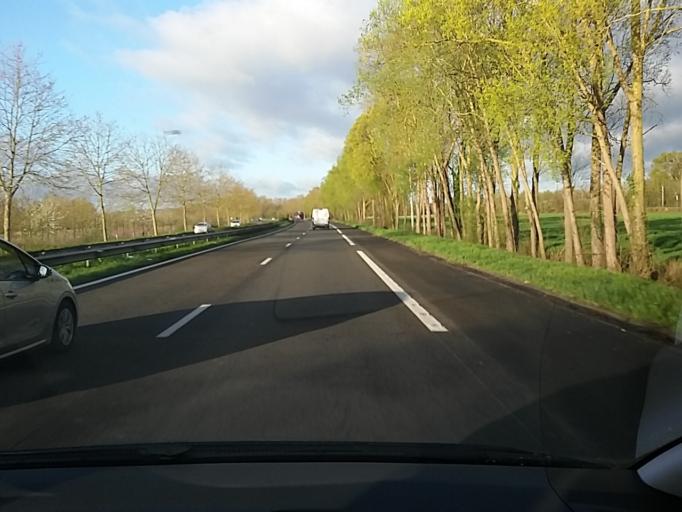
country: FR
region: Picardie
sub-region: Departement de l'Oise
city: Le Meux
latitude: 49.3500
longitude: 2.7464
